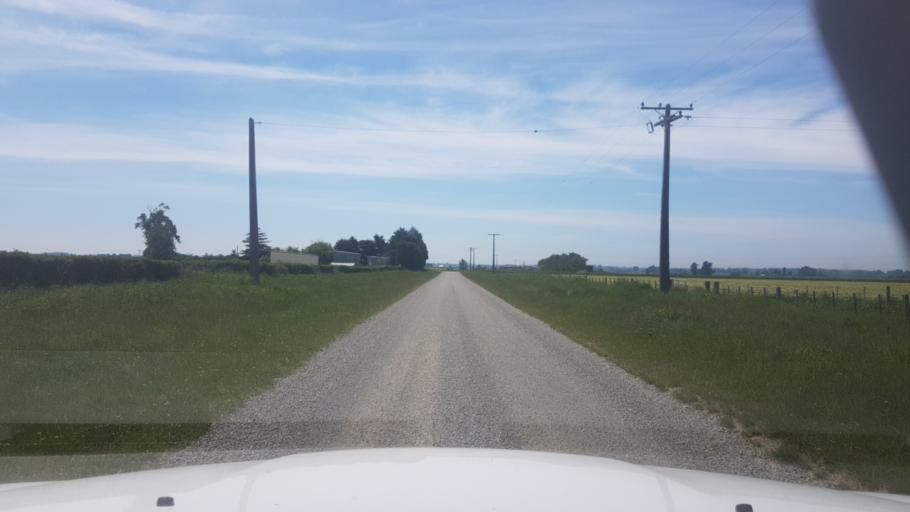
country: NZ
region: Canterbury
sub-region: Timaru District
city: Pleasant Point
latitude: -44.2446
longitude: 171.1977
